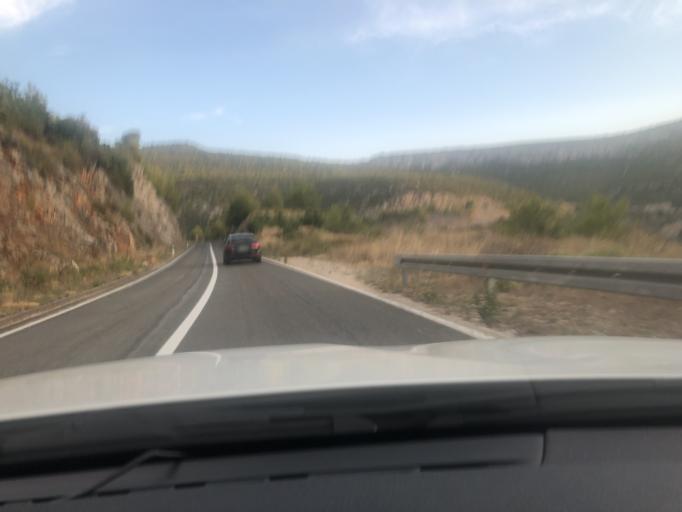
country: HR
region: Splitsko-Dalmatinska
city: Stari Grad
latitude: 43.1710
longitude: 16.5637
